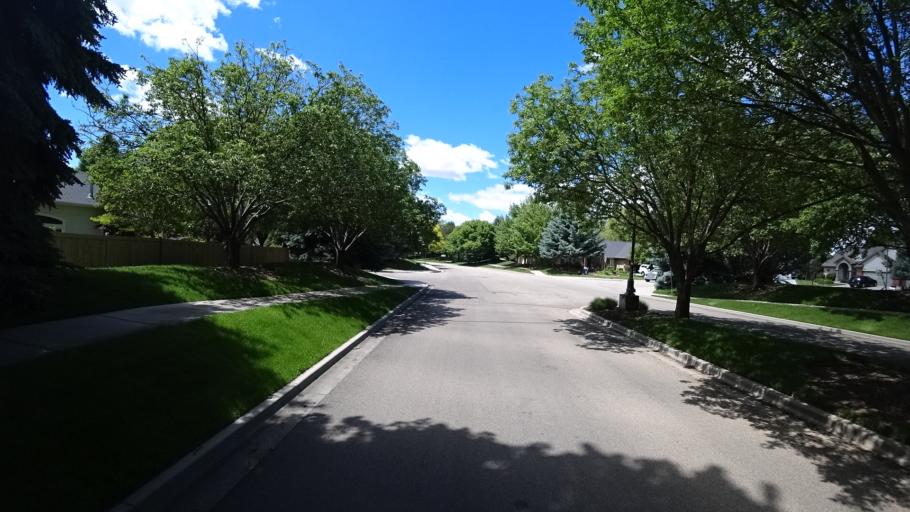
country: US
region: Idaho
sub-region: Ada County
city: Eagle
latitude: 43.6587
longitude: -116.3551
